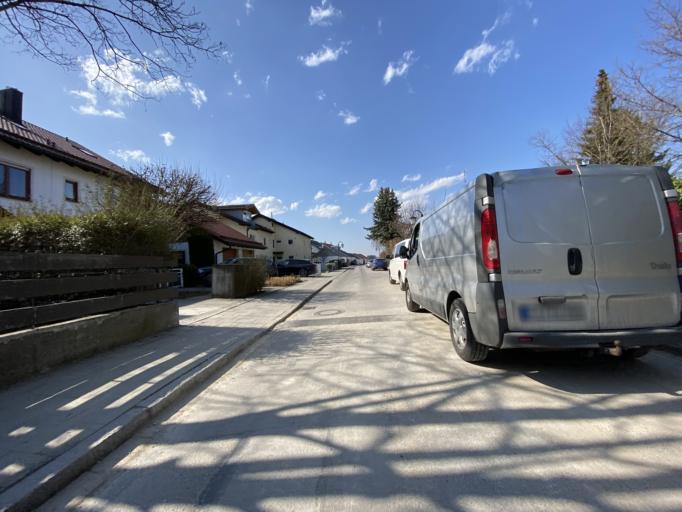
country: DE
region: Bavaria
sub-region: Upper Bavaria
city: Aschheim
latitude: 48.1539
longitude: 11.6859
